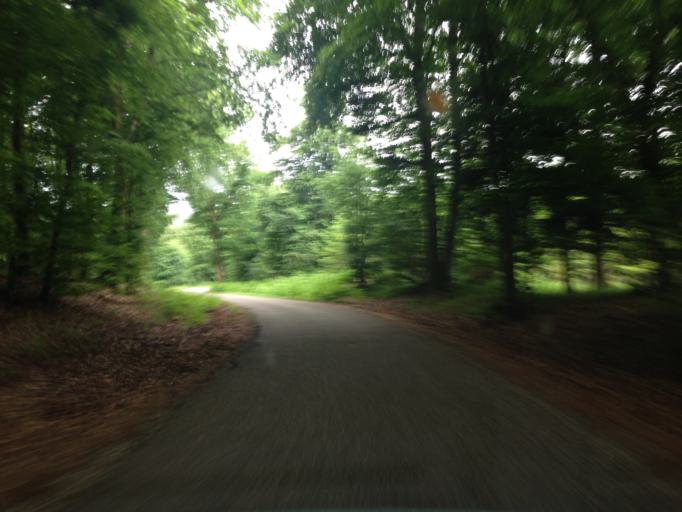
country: FR
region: Alsace
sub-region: Departement du Bas-Rhin
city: Neuwiller-les-Saverne
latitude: 48.8482
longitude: 7.3613
